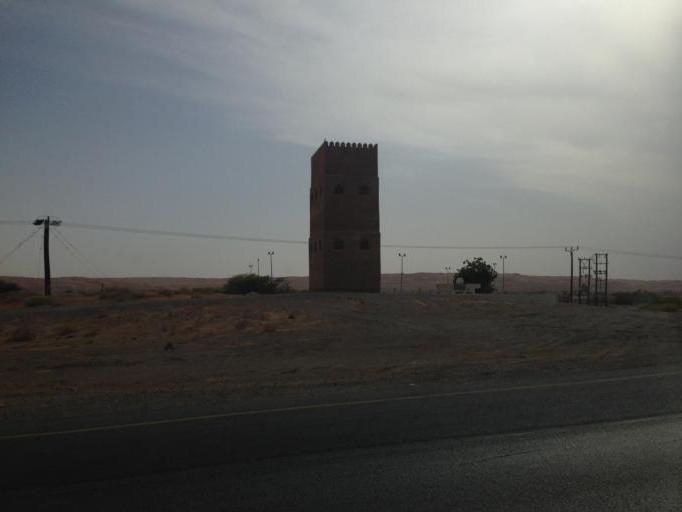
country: OM
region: Ash Sharqiyah
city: Al Qabil
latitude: 22.5086
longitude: 58.7424
